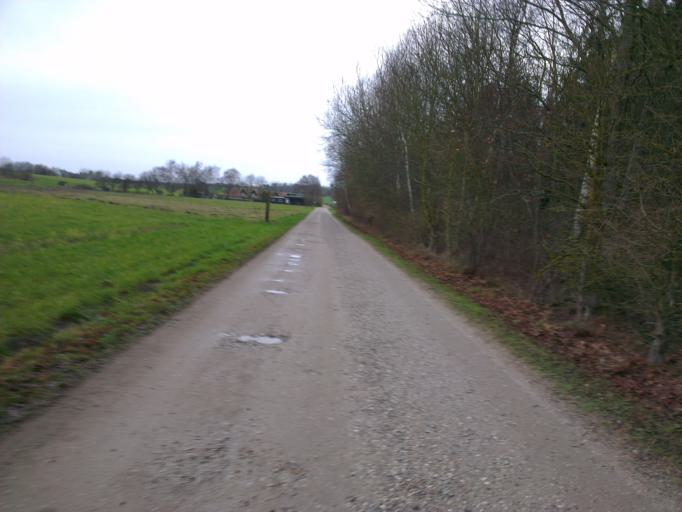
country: DK
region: Capital Region
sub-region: Frederikssund Kommune
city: Jaegerspris
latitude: 55.8403
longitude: 12.0134
